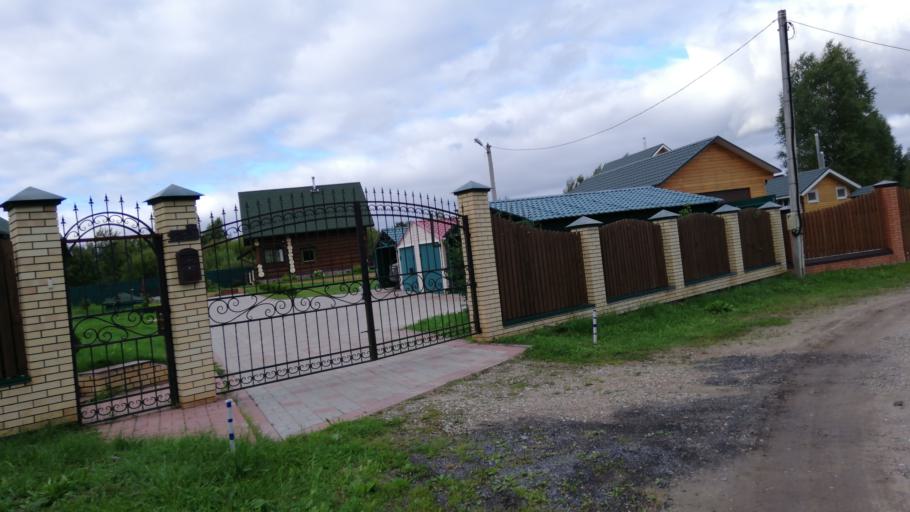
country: RU
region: Jaroslavl
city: Konstantinovskiy
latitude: 57.8024
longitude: 39.7161
